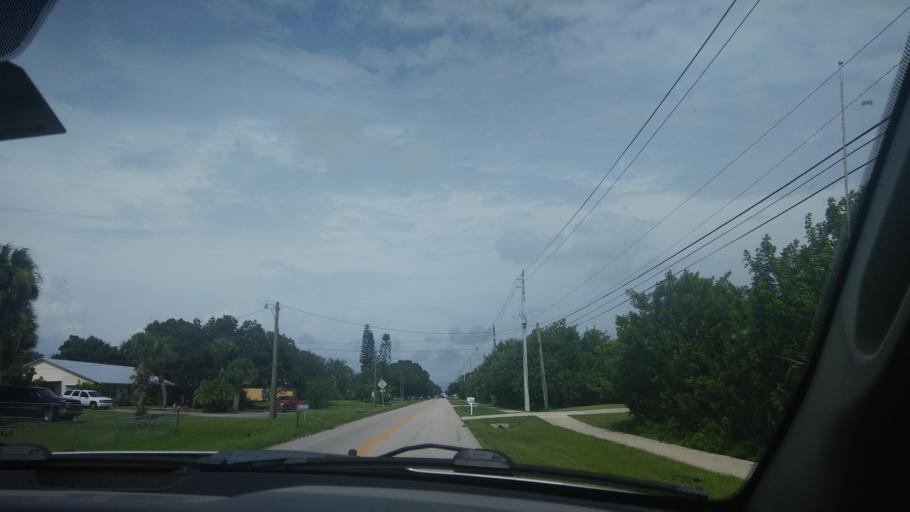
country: US
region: Florida
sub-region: Indian River County
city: Sebastian
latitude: 27.7526
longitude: -80.5165
